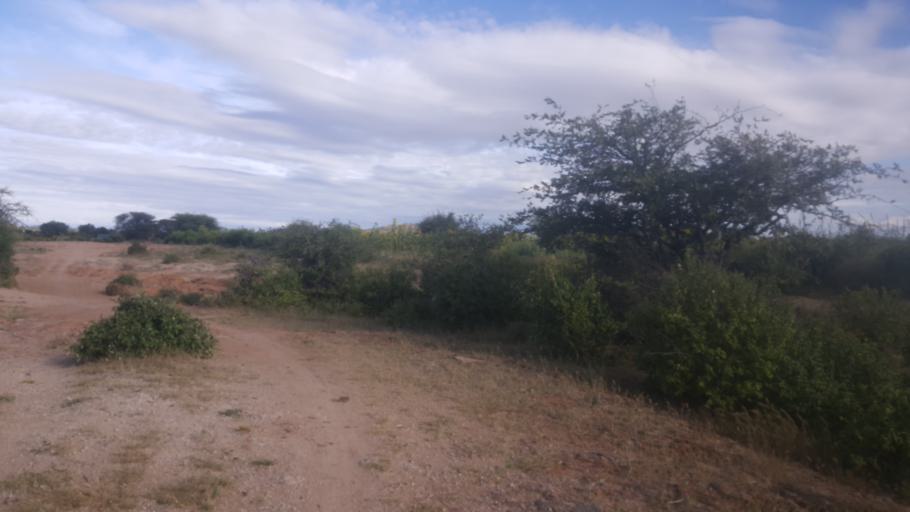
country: TZ
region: Dodoma
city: Dodoma
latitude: -6.0974
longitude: 35.5311
